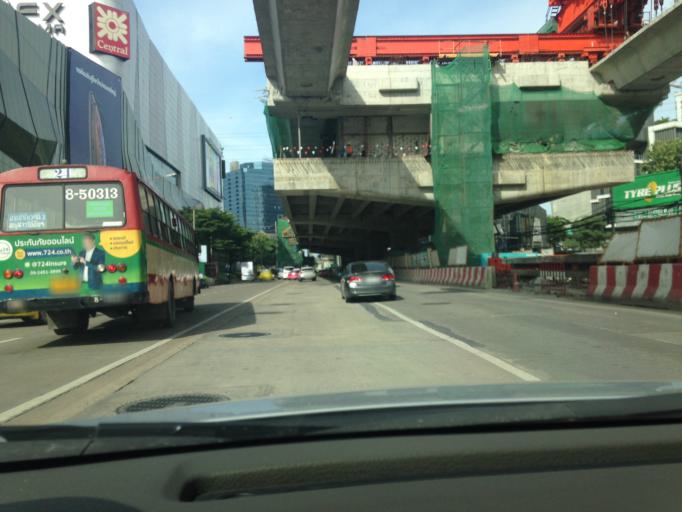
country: TH
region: Bangkok
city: Chatuchak
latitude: 13.8158
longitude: 100.5614
